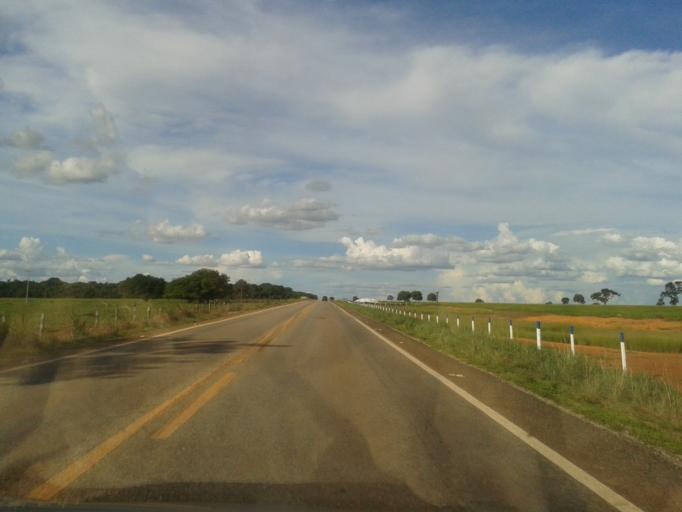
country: BR
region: Goias
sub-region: Mozarlandia
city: Mozarlandia
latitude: -14.3381
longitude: -50.4171
